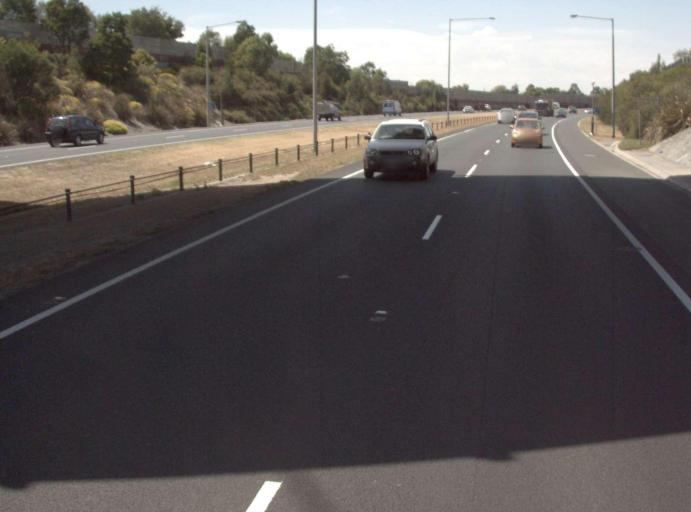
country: AU
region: Victoria
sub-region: Casey
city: Narre Warren North
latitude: -38.0009
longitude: 145.2929
